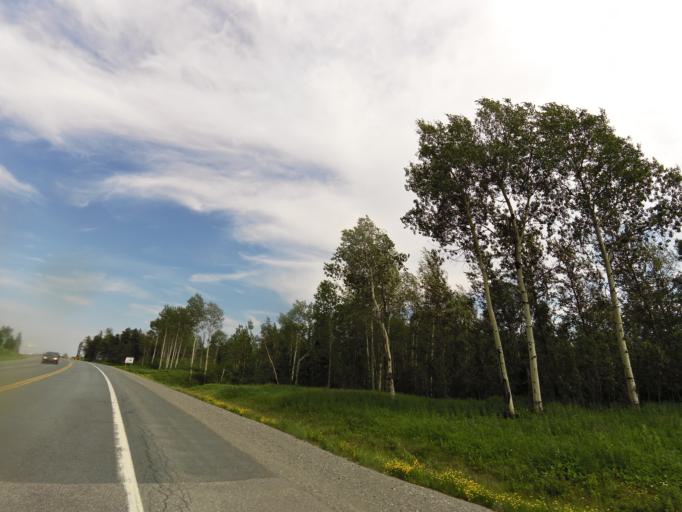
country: CA
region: Quebec
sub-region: Abitibi-Temiscamingue
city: Malartic
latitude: 48.2263
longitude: -78.3947
